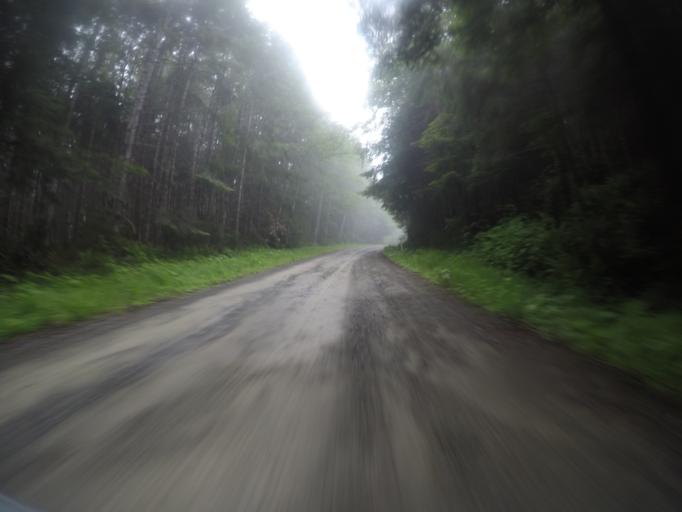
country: US
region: California
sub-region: Humboldt County
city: Westhaven-Moonstone
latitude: 41.2354
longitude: -123.9907
